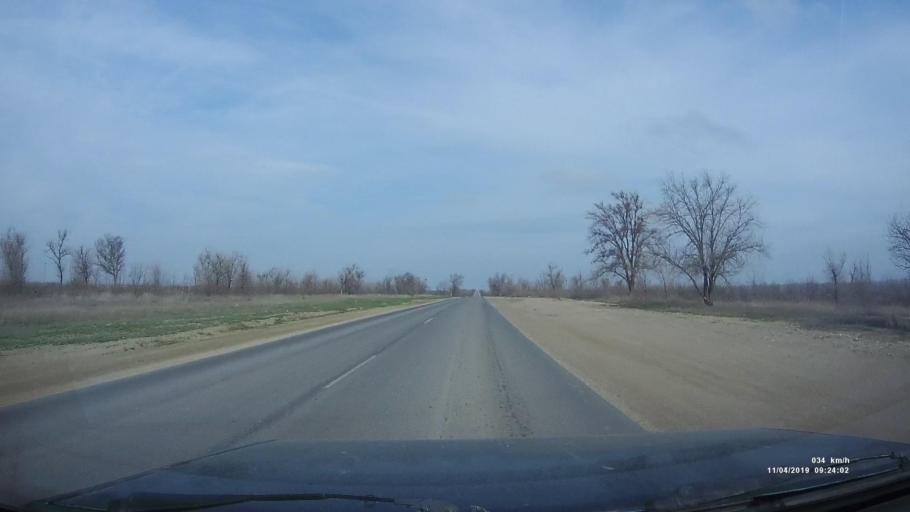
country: RU
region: Rostov
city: Staraya Stanitsa
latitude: 48.2463
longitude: 40.3858
